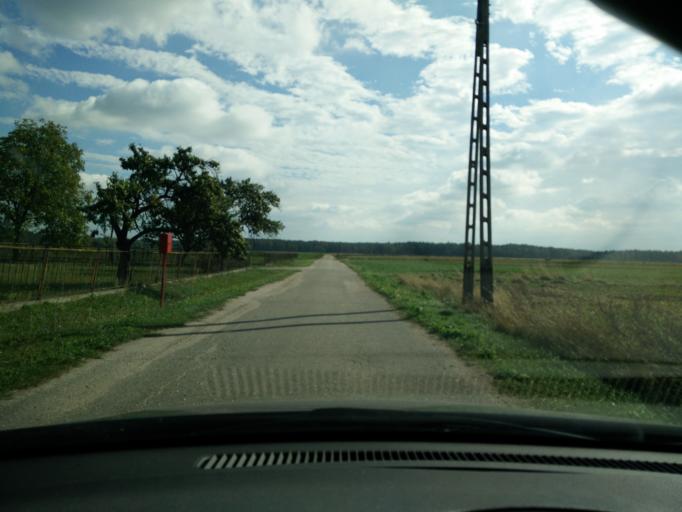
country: PL
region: Greater Poland Voivodeship
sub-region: Powiat sredzki
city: Dominowo
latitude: 52.2872
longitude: 17.3860
